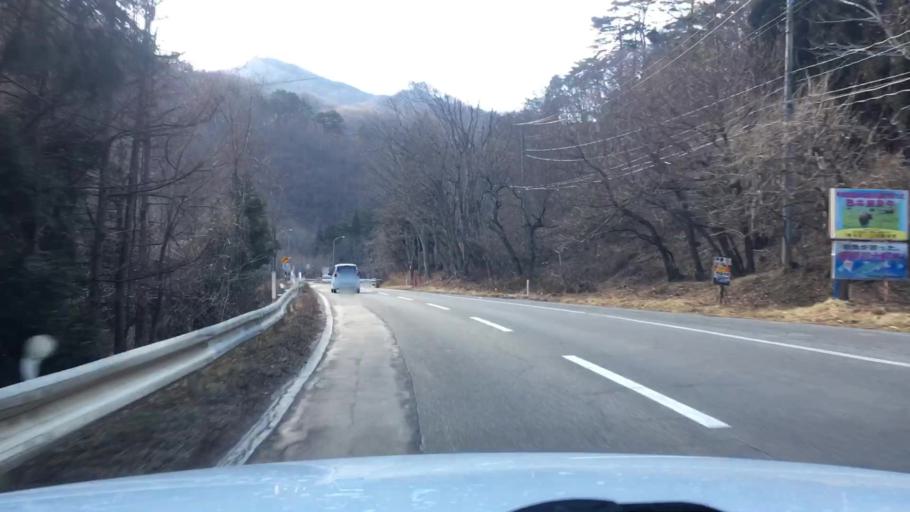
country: JP
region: Iwate
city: Miyako
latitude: 39.5970
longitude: 141.7222
